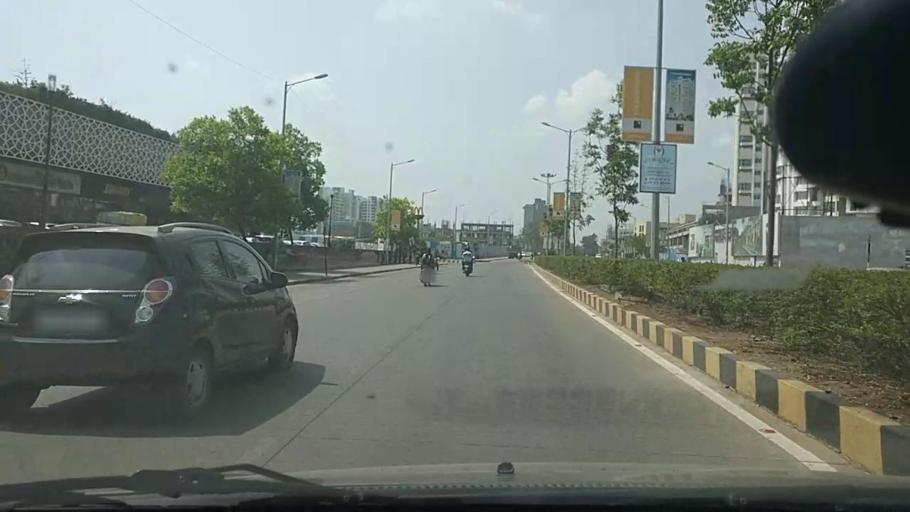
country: IN
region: Maharashtra
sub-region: Pune Division
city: Pimpri
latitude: 18.5696
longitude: 73.7749
